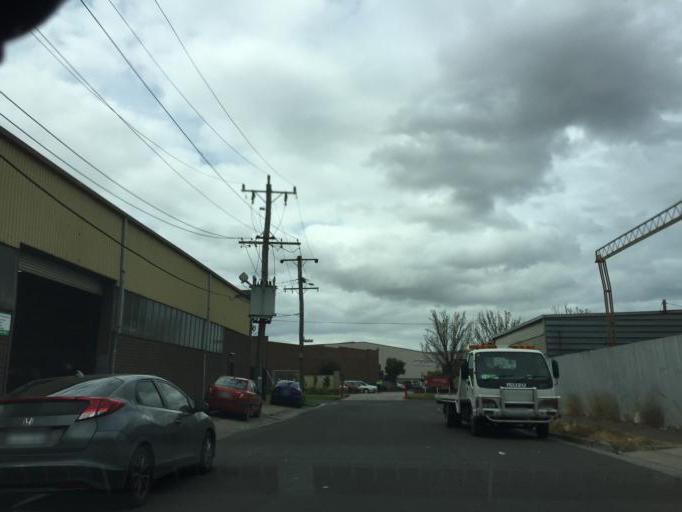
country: AU
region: Victoria
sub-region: Brimbank
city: Brooklyn
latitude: -37.8002
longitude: 144.8398
